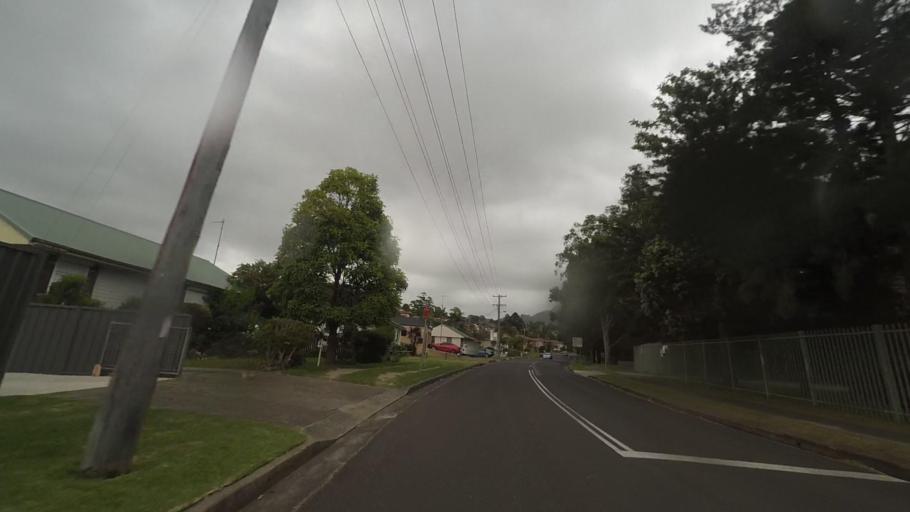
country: AU
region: New South Wales
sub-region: Wollongong
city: Cordeaux Heights
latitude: -34.4521
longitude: 150.8409
